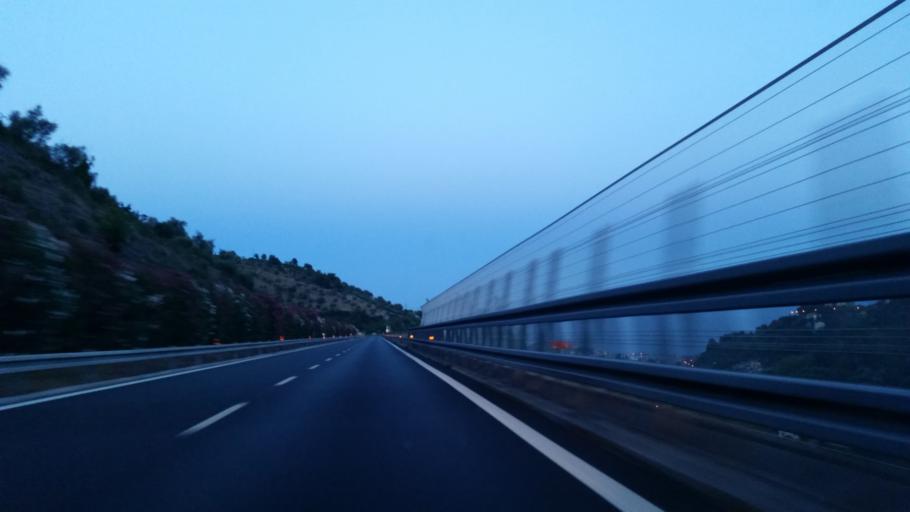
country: IT
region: Liguria
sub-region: Provincia di Imperia
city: San Remo
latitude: 43.8385
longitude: 7.7580
